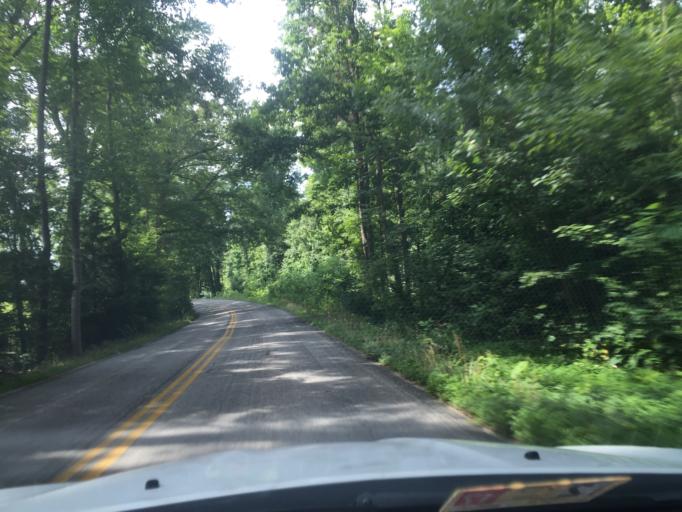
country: US
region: Virginia
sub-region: Charles City County
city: Charles City
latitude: 37.3947
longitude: -77.0164
